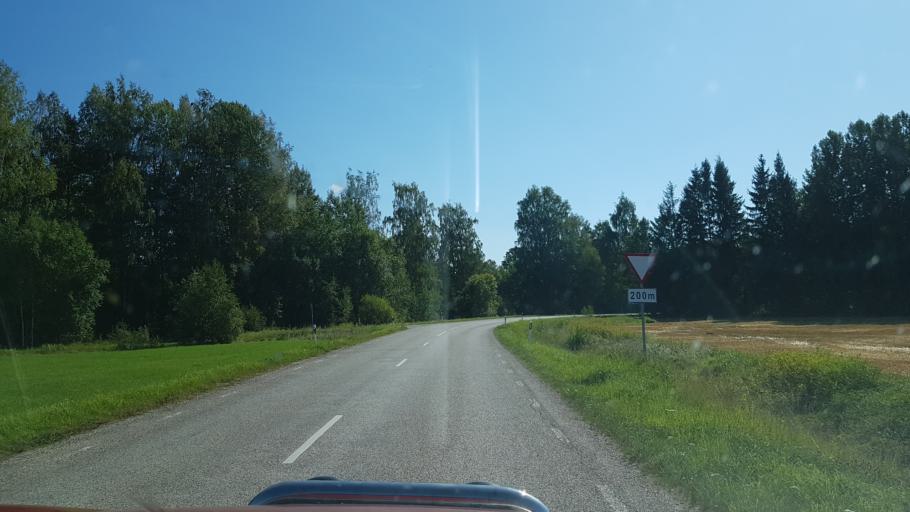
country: EE
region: Polvamaa
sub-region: Raepina vald
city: Rapina
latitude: 58.2121
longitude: 27.2544
